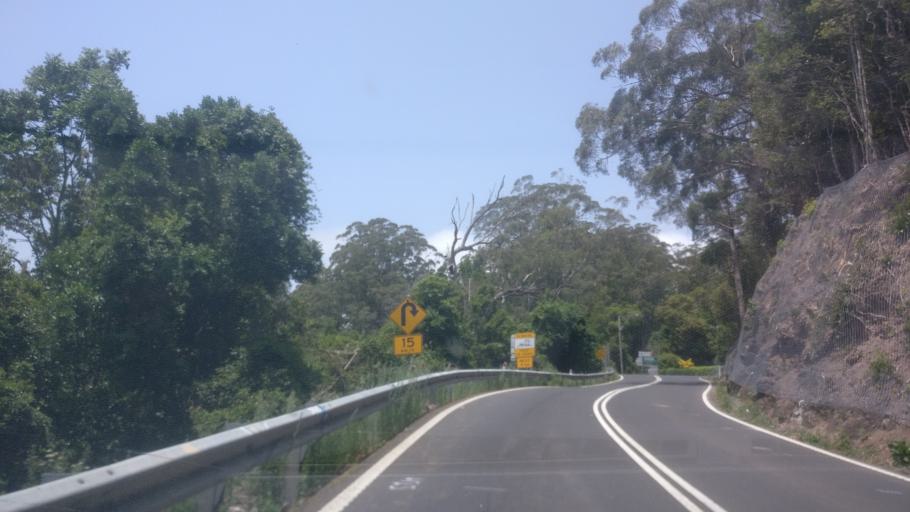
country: AU
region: New South Wales
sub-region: Shoalhaven Shire
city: Kangaroo Valley
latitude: -34.7892
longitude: 150.5647
